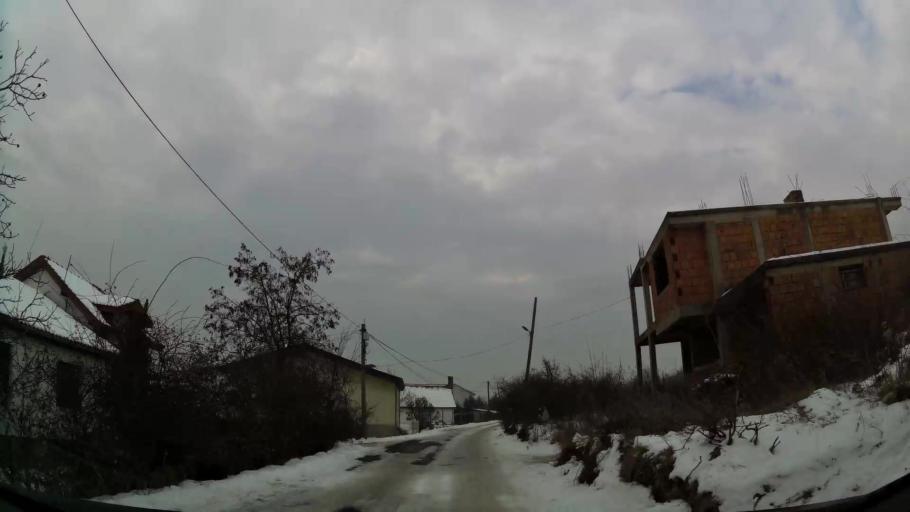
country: MK
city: Kondovo
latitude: 42.0381
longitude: 21.3439
